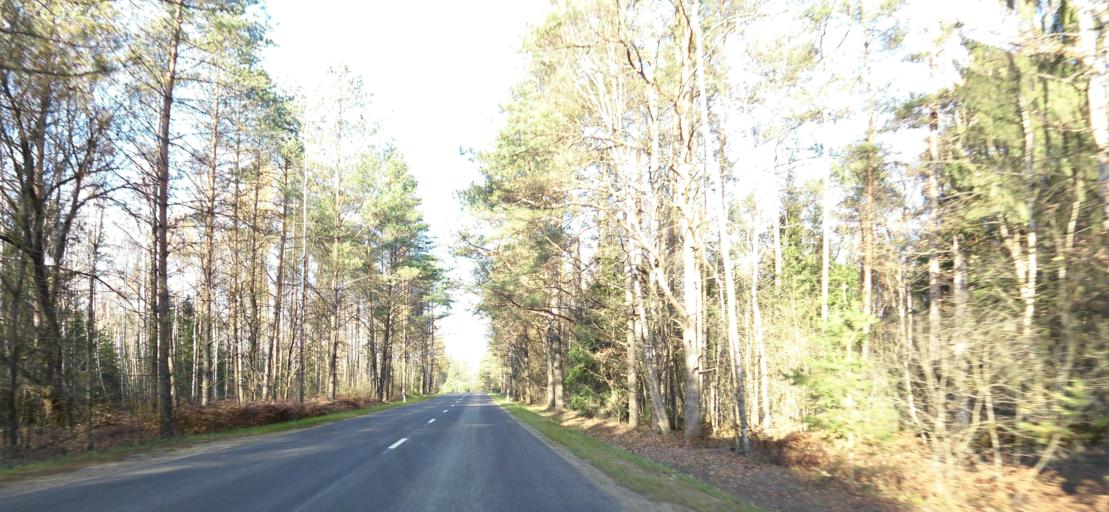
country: LT
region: Vilnius County
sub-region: Trakai
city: Rudiskes
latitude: 54.5092
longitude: 24.8811
